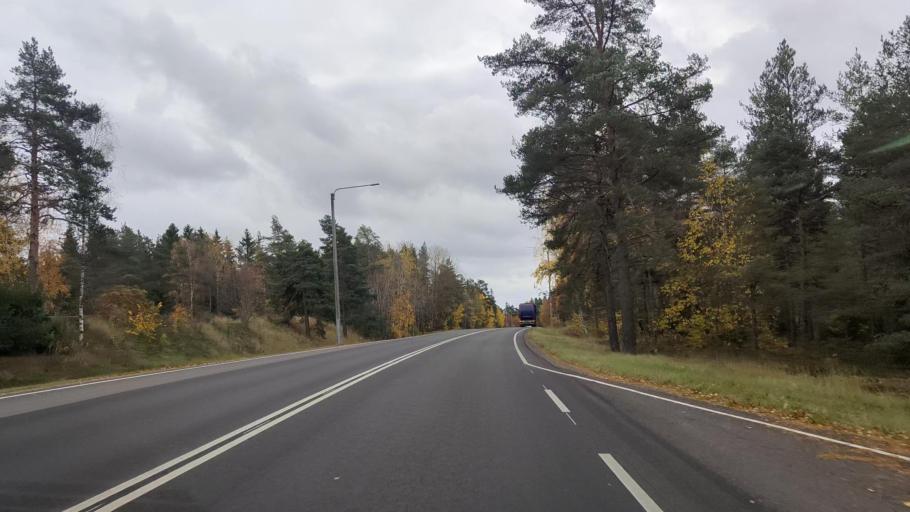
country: FI
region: Varsinais-Suomi
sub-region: Turku
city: Kaarina
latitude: 60.4509
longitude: 22.3724
